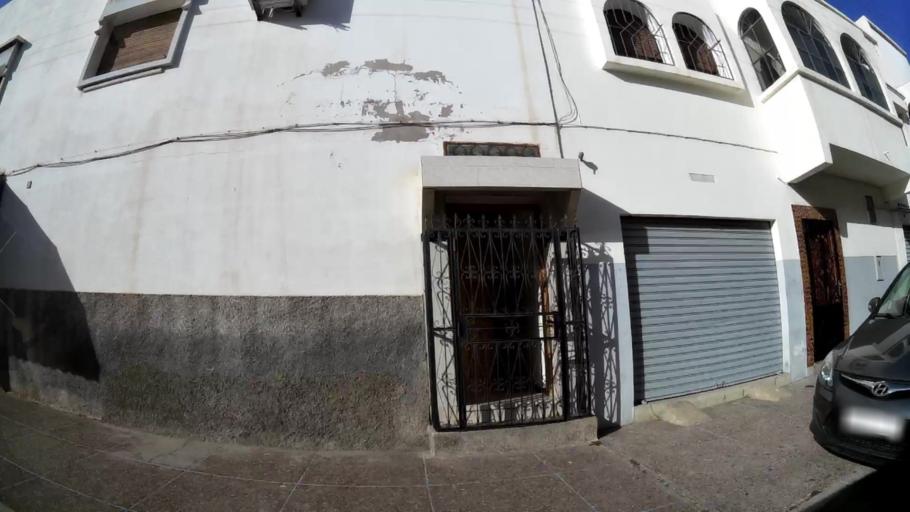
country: MA
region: Souss-Massa-Draa
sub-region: Agadir-Ida-ou-Tnan
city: Agadir
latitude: 30.4297
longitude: -9.5809
